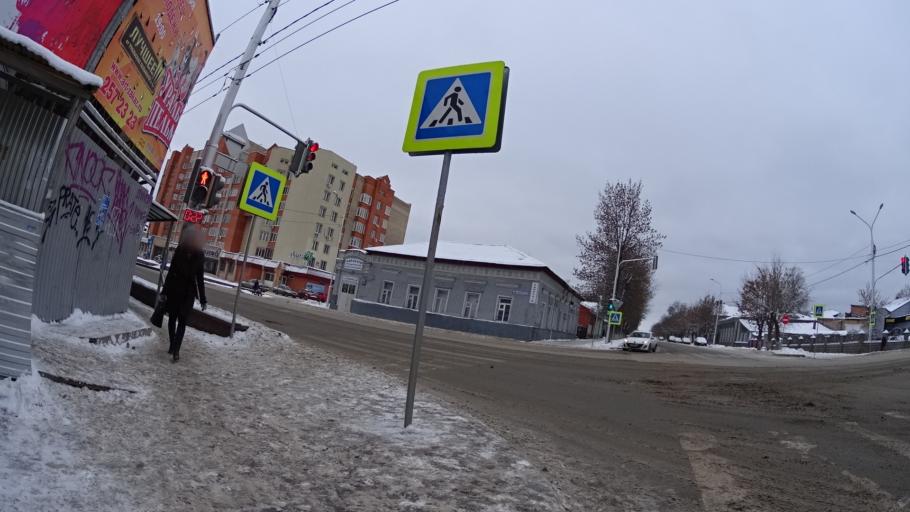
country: RU
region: Bashkortostan
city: Ufa
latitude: 54.7236
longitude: 55.9368
